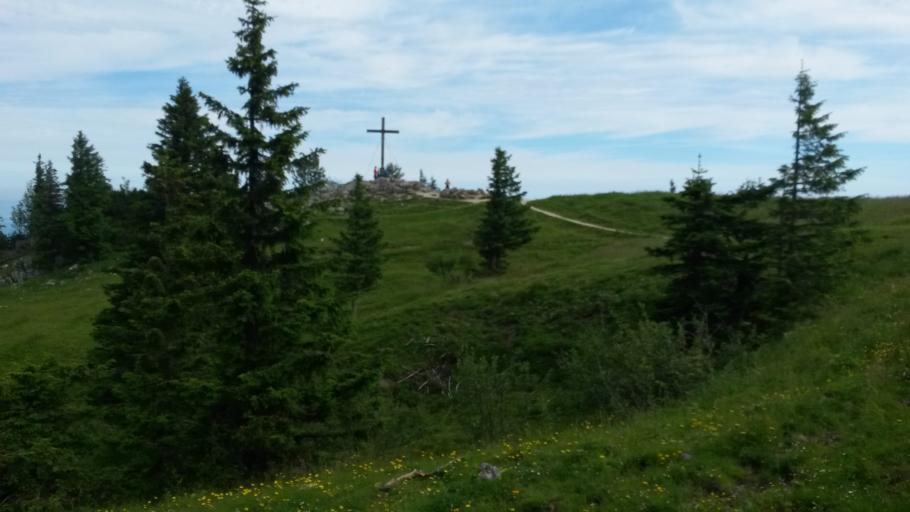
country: DE
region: Bavaria
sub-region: Upper Bavaria
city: Aschau im Chiemgau
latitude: 47.7549
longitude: 12.3563
